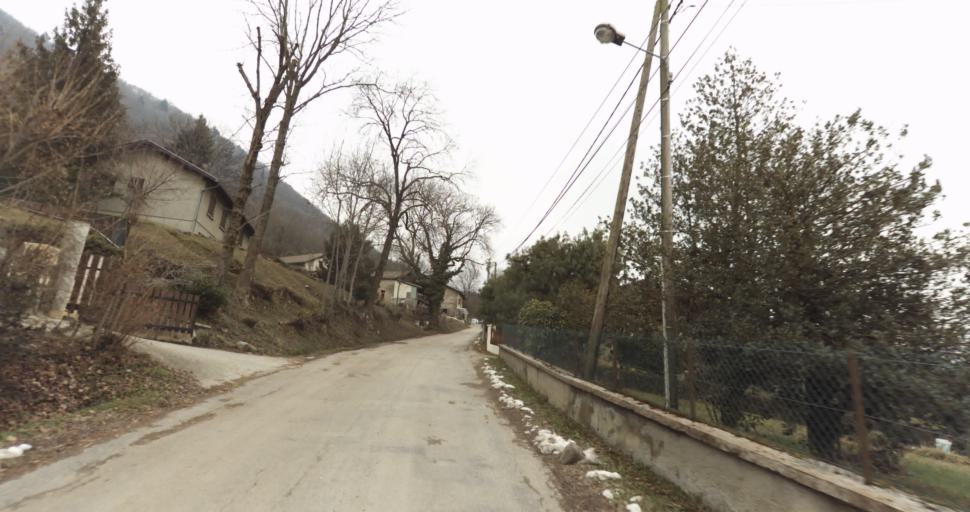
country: FR
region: Rhone-Alpes
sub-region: Departement de l'Isere
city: Vif
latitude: 45.0264
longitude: 5.6640
